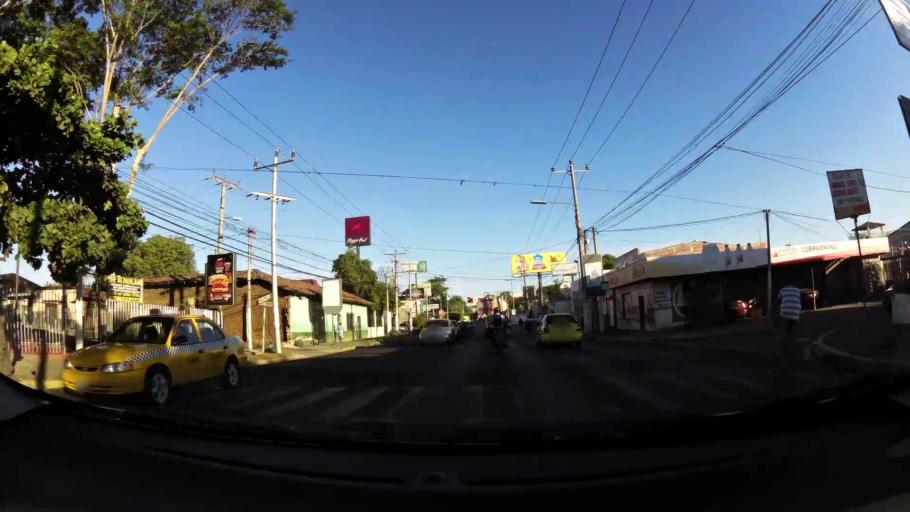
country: SV
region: San Miguel
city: San Miguel
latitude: 13.4792
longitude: -88.1846
